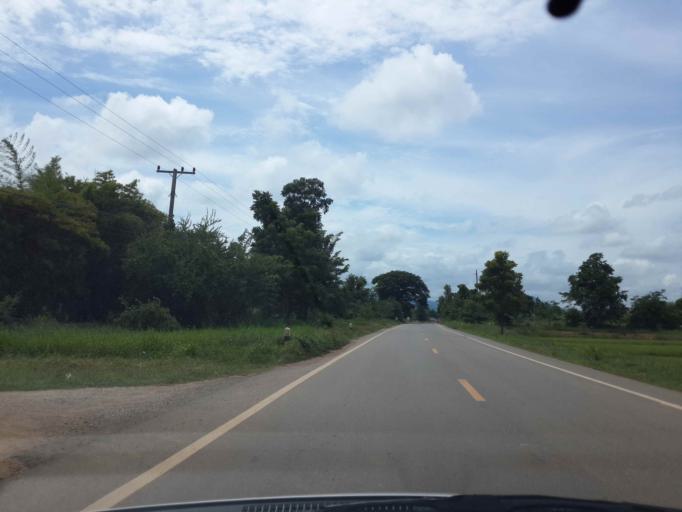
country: TH
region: Ratchaburi
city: Pak Tho
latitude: 13.3657
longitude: 99.7013
